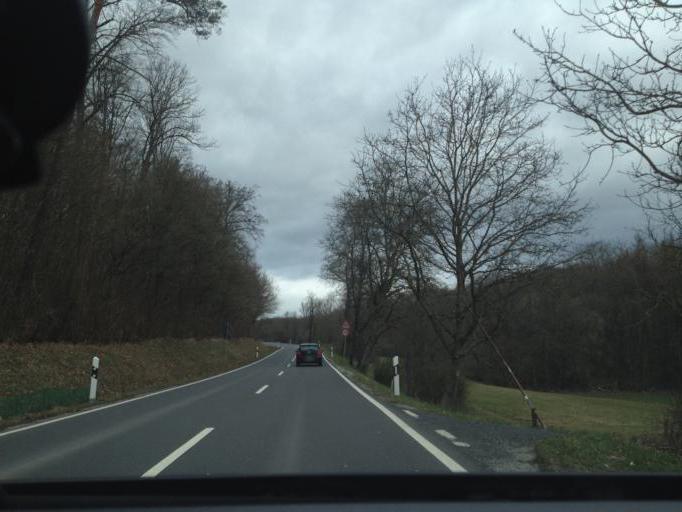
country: DE
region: Bavaria
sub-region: Regierungsbezirk Unterfranken
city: Wuerzburg
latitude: 49.7360
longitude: 9.8758
